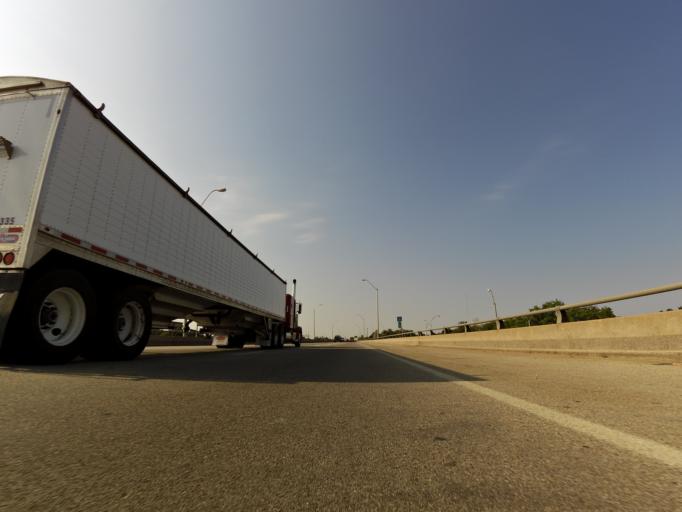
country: US
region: Kansas
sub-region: Sedgwick County
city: Wichita
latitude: 37.7073
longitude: -97.3193
